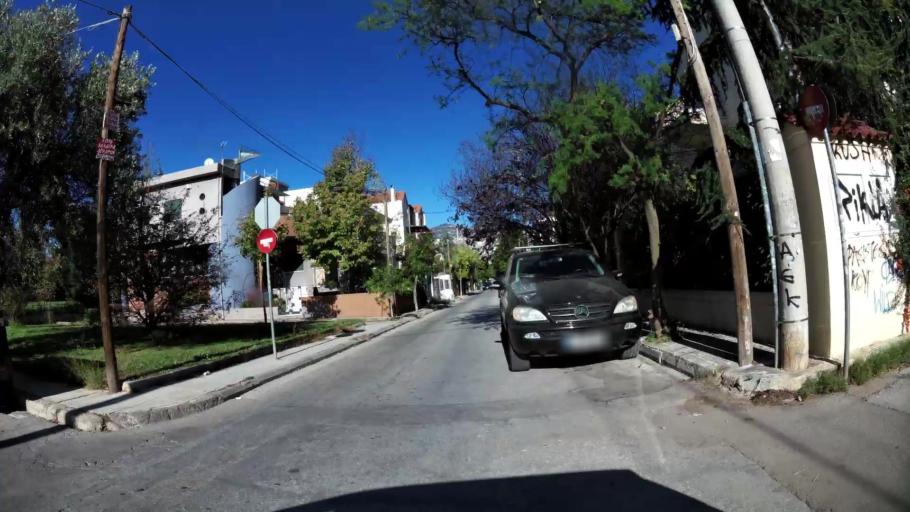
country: GR
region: Attica
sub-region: Nomarchia Athinas
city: Melissia
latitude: 38.0416
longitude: 23.8381
